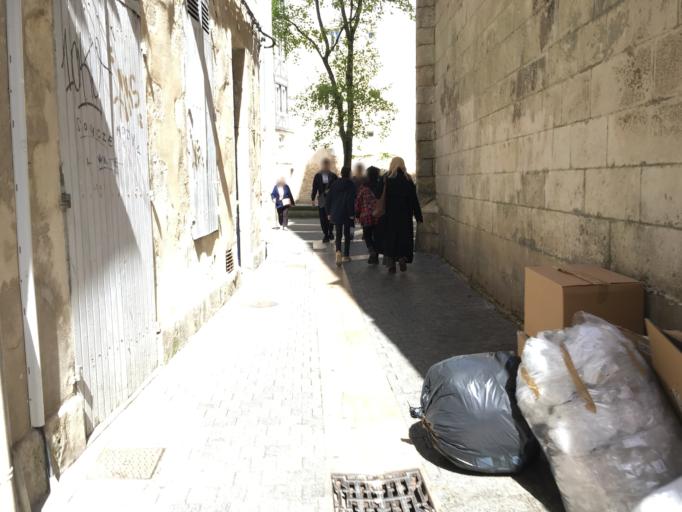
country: FR
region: Poitou-Charentes
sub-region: Departement de la Charente-Maritime
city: La Rochelle
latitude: 46.1588
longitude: -1.1507
